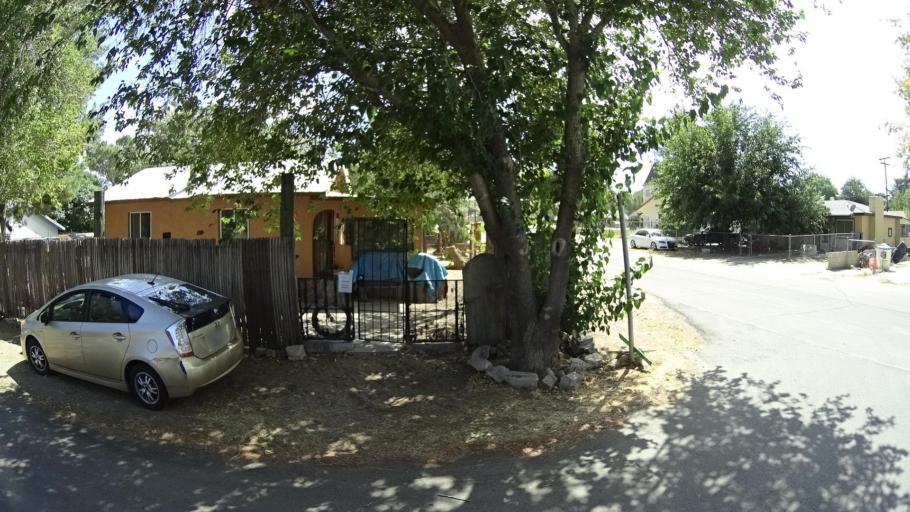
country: MX
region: Baja California
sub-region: Tecate
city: Cereso del Hongo
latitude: 32.6198
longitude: -116.1872
